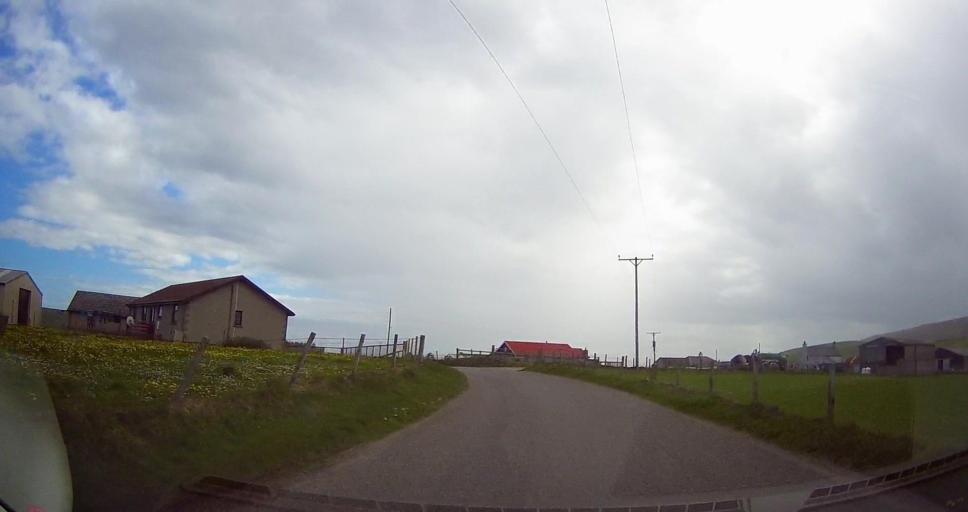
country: GB
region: Scotland
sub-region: Shetland Islands
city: Sandwick
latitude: 59.9138
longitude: -1.3239
